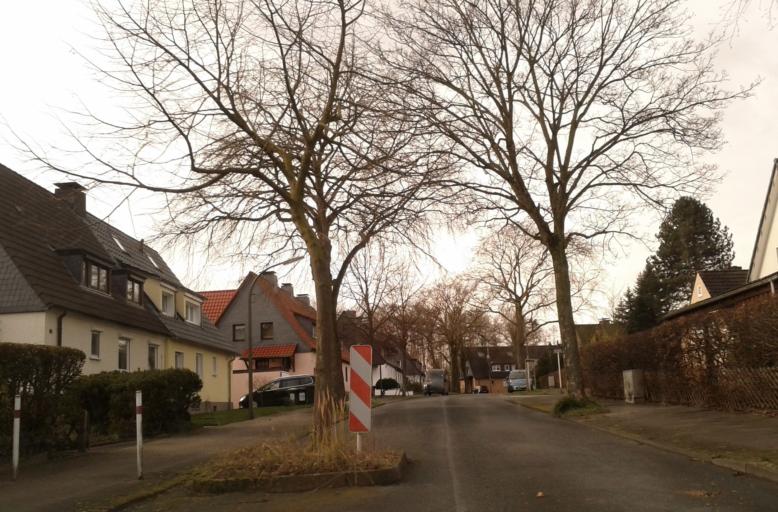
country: DE
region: North Rhine-Westphalia
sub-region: Regierungsbezirk Arnsberg
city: Dortmund
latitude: 51.5522
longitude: 7.5002
